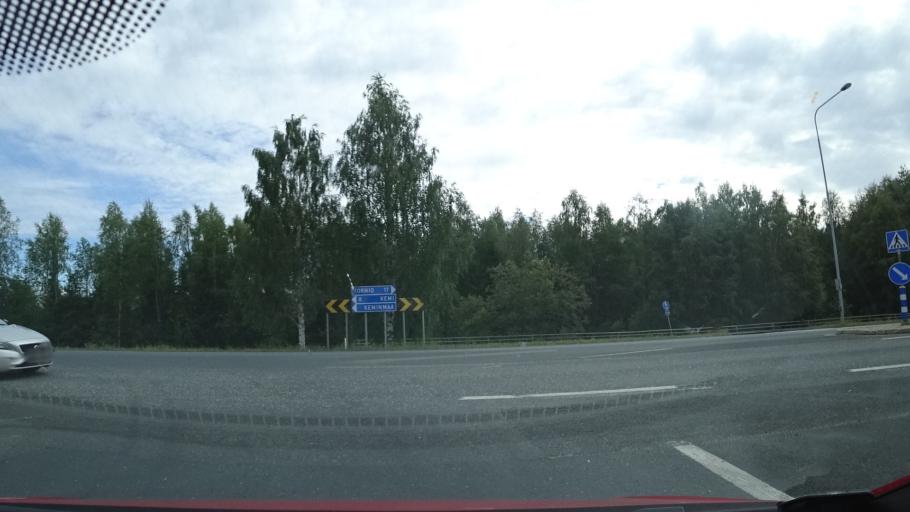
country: FI
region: Lapland
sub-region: Kemi-Tornio
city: Keminmaa
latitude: 65.8020
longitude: 24.4907
